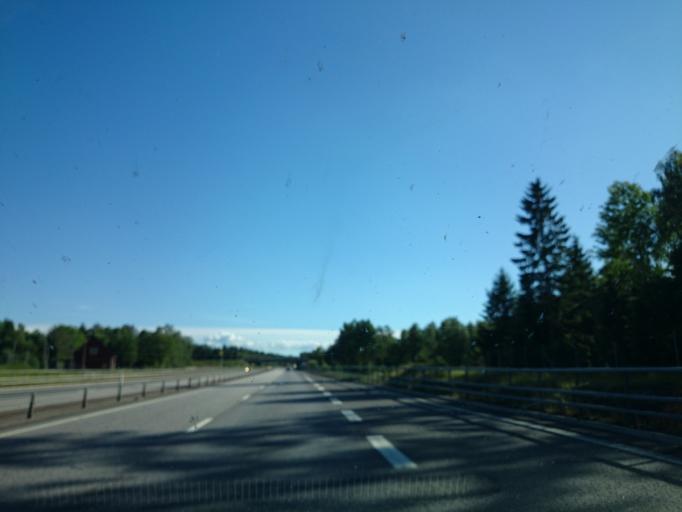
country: SE
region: Kronoberg
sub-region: Markaryds Kommun
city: Markaryd
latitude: 56.4642
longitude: 13.6292
